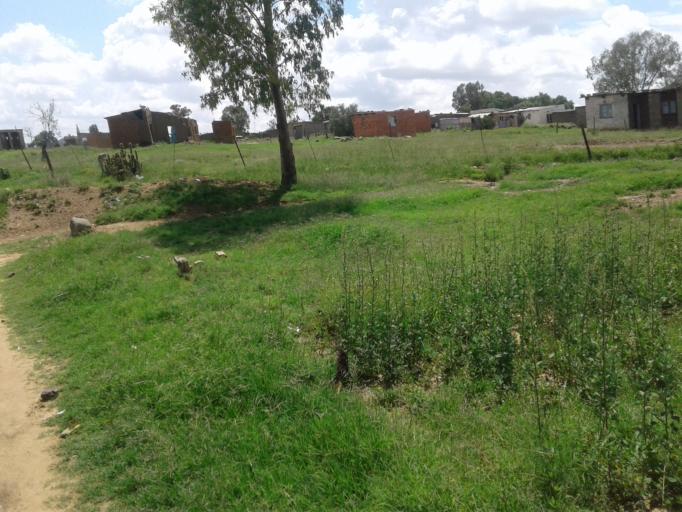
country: LS
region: Mafeteng
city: Mafeteng
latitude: -29.7583
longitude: 27.1112
